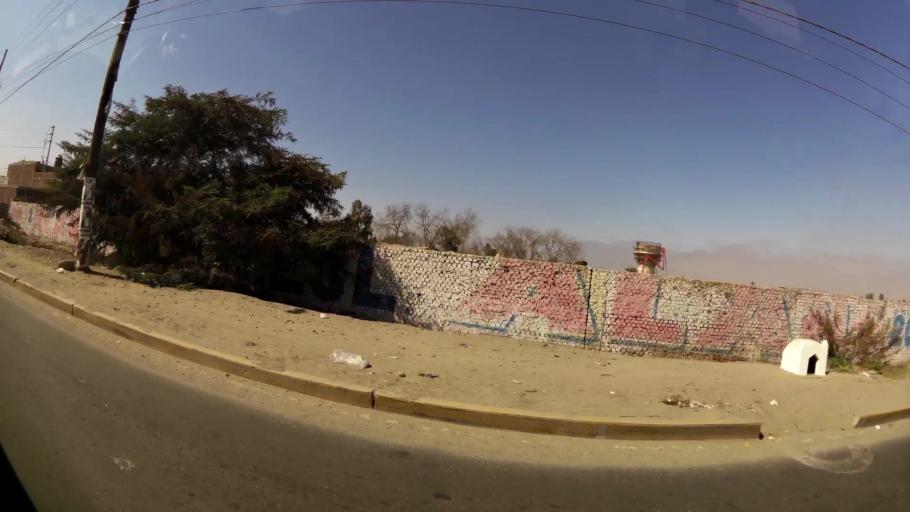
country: PE
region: Ica
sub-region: Provincia de Ica
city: Ica
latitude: -14.0584
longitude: -75.7109
